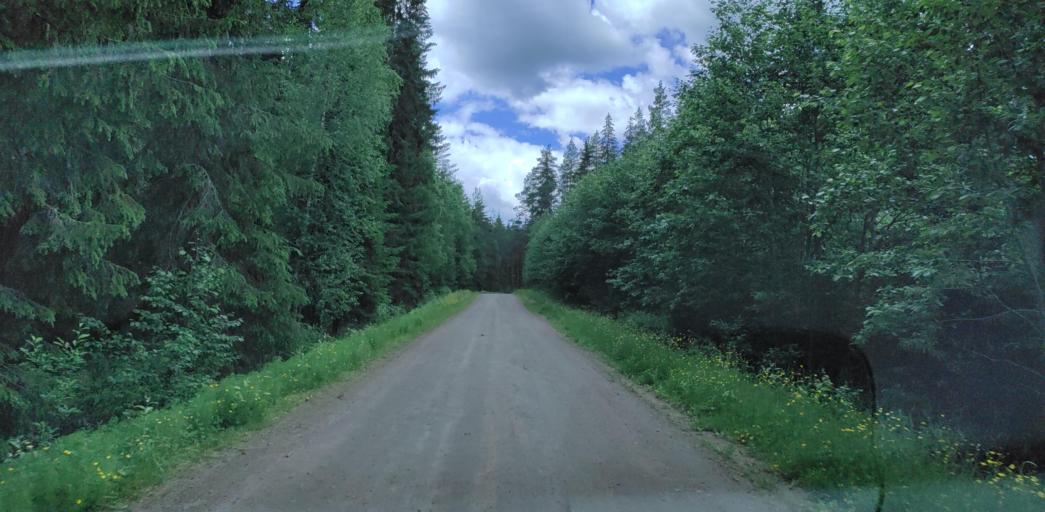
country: SE
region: Vaermland
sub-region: Hagfors Kommun
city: Ekshaerad
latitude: 60.0847
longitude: 13.4434
